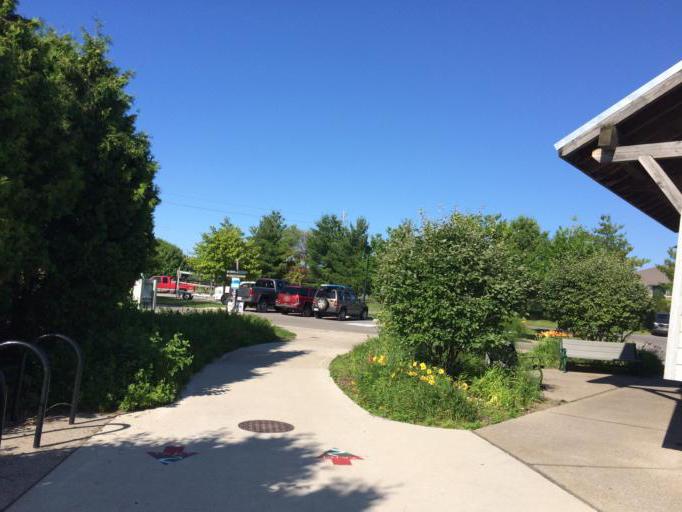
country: US
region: Michigan
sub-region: Grand Traverse County
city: Traverse City
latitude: 44.7571
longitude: -85.6112
